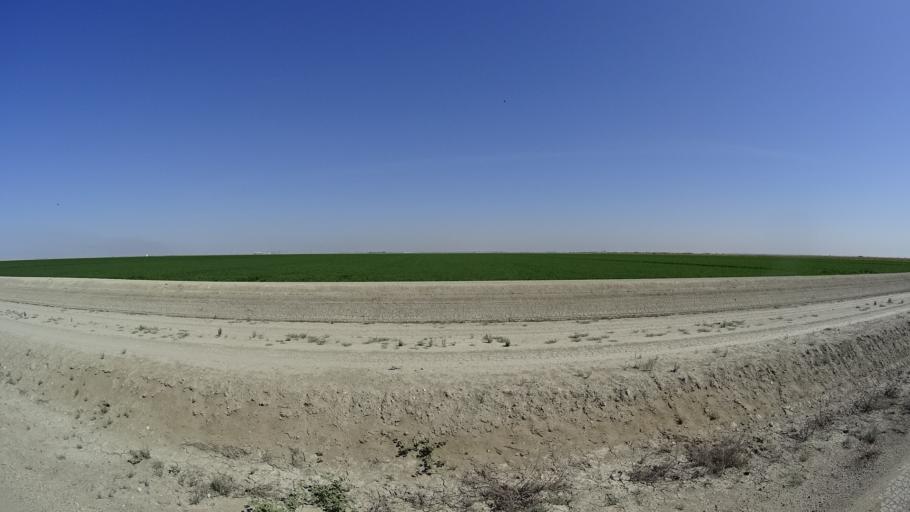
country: US
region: California
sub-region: Tulare County
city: Alpaugh
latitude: 35.9781
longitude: -119.5654
